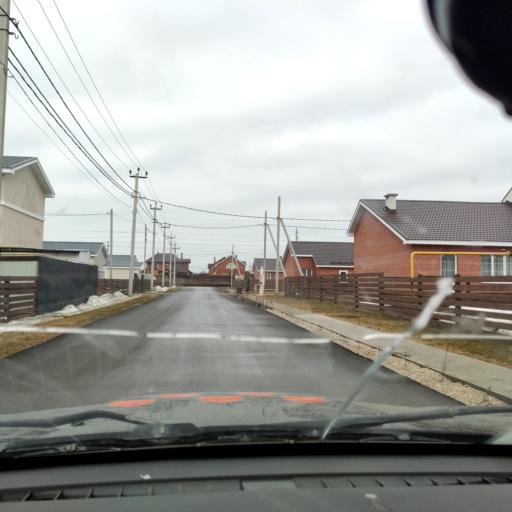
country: RU
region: Samara
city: Podstepki
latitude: 53.5791
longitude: 49.0849
